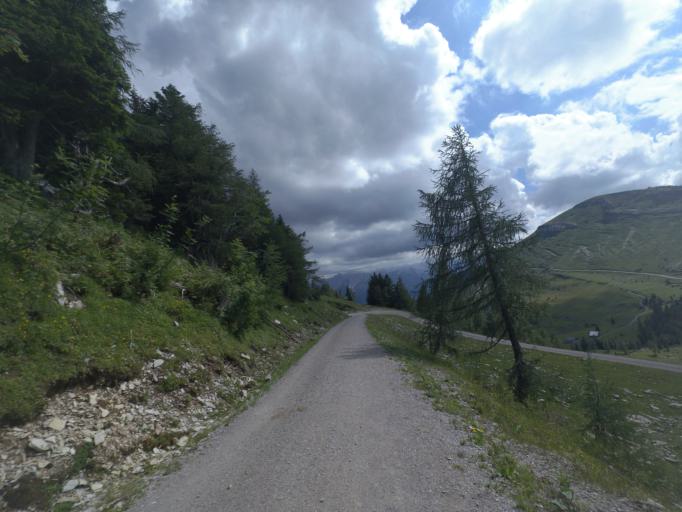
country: AT
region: Salzburg
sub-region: Politischer Bezirk Salzburg-Umgebung
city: Hintersee
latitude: 47.6501
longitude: 13.2892
